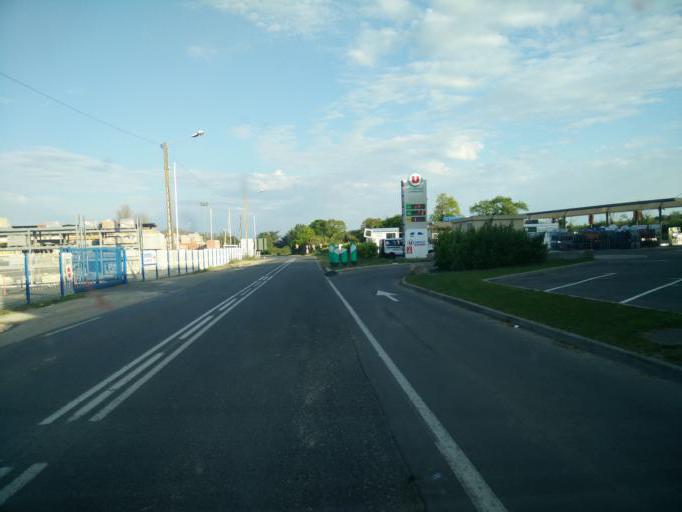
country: FR
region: Brittany
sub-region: Departement des Cotes-d'Armor
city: Erquy
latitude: 48.6228
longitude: -2.4401
